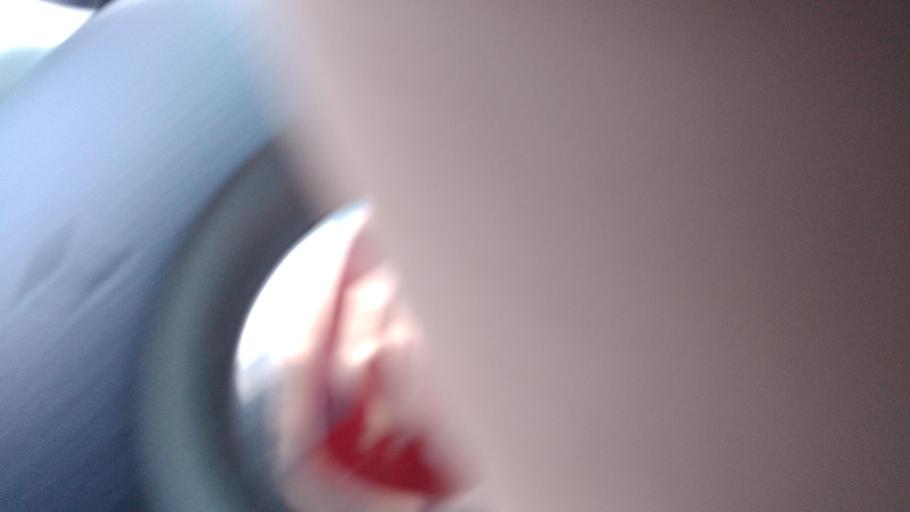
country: UY
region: Canelones
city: Tala
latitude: -34.2042
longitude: -55.7400
